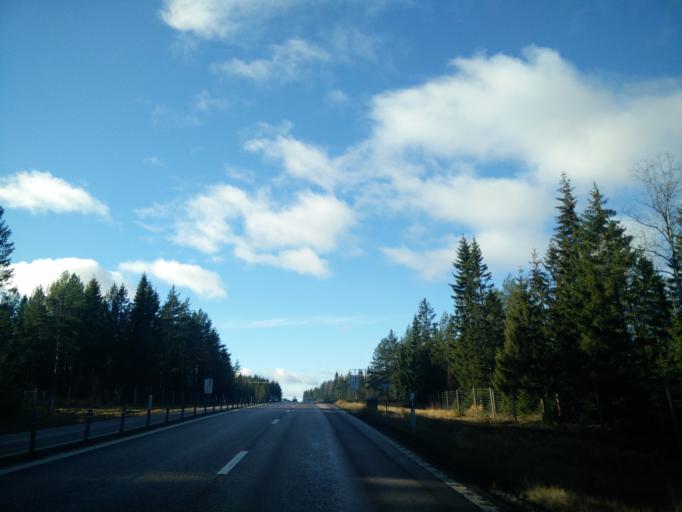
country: SE
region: Vaesternorrland
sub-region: Timra Kommun
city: Soraker
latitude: 62.5345
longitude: 17.5271
